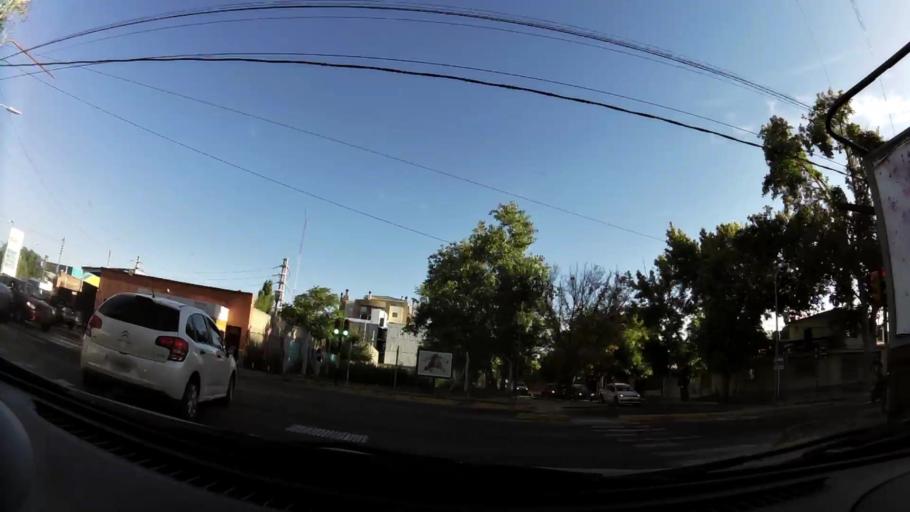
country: AR
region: Mendoza
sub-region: Departamento de Godoy Cruz
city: Godoy Cruz
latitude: -32.9085
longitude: -68.8392
